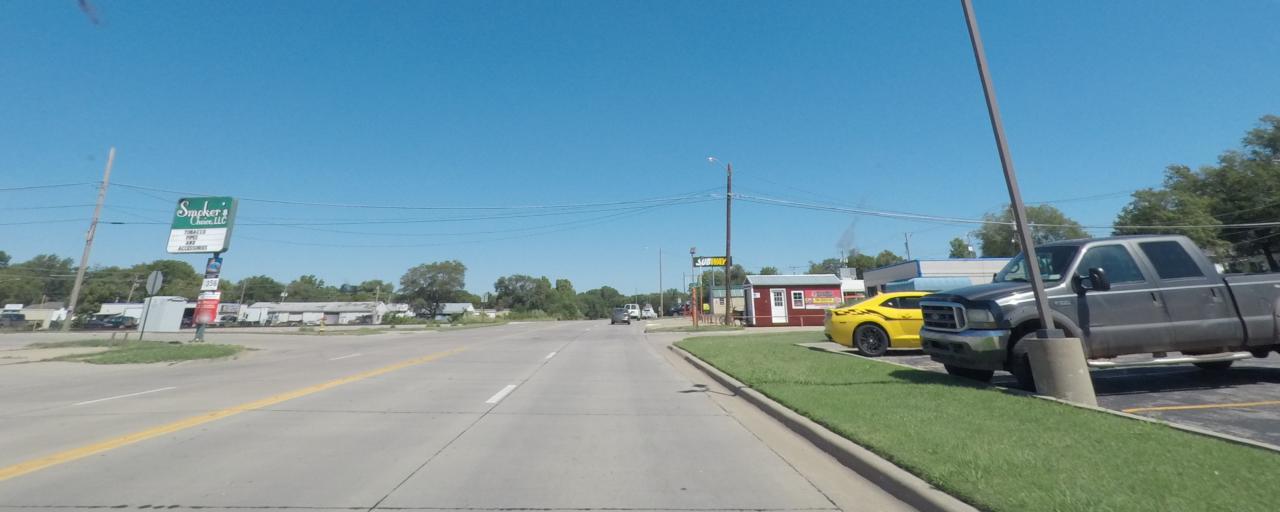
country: US
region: Kansas
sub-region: Sumner County
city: Wellington
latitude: 37.2713
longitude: -97.4020
